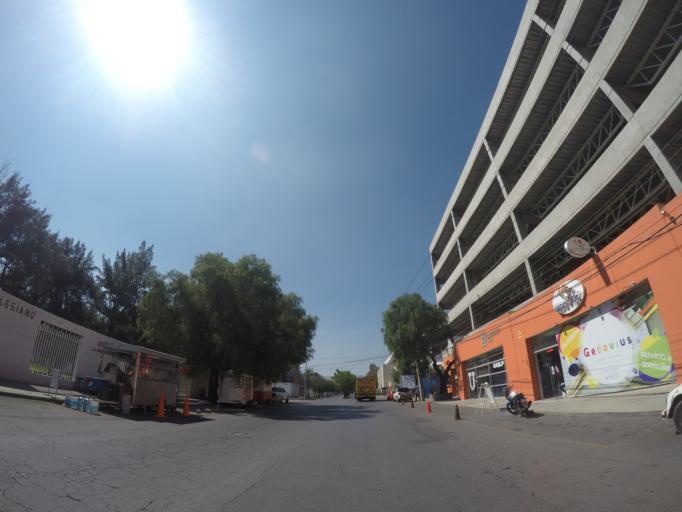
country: MX
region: San Luis Potosi
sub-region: San Luis Potosi
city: San Luis Potosi
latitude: 22.1450
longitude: -101.0140
